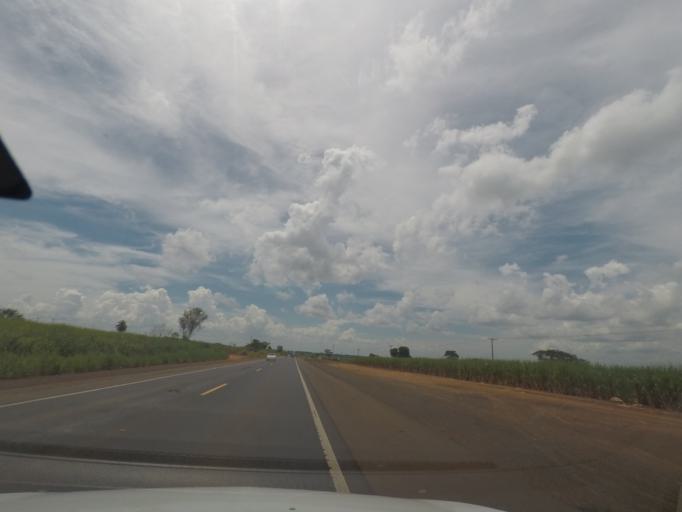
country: BR
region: Sao Paulo
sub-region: Barretos
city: Barretos
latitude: -20.3876
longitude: -48.6406
